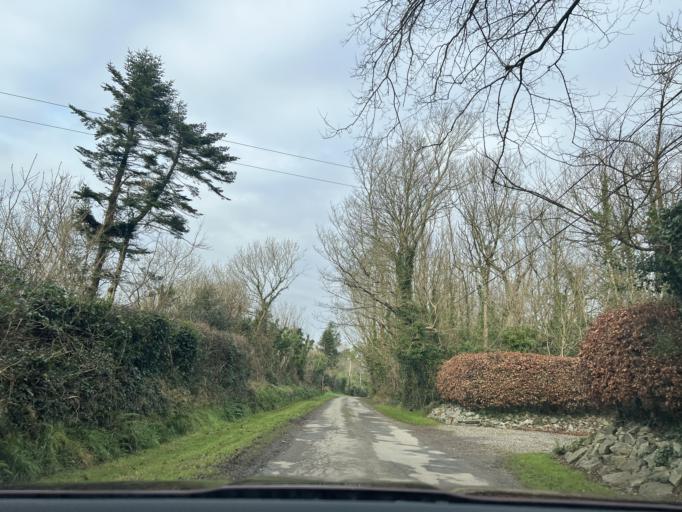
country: IE
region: Leinster
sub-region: Loch Garman
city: Loch Garman
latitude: 52.3712
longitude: -6.5362
